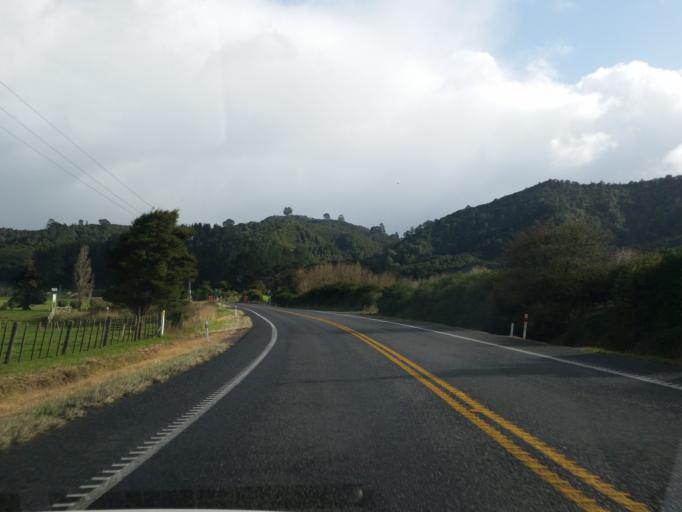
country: NZ
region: Auckland
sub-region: Auckland
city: Pukekohe East
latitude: -37.2133
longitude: 175.0843
